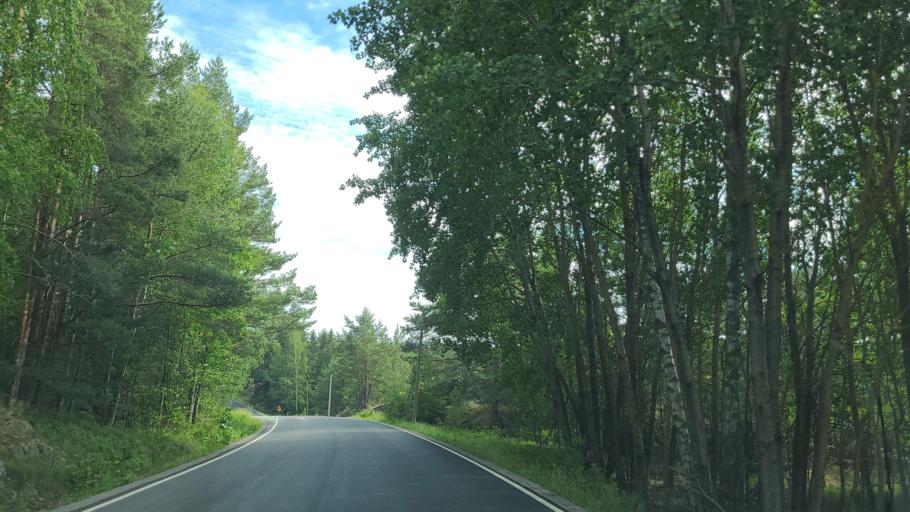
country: FI
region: Varsinais-Suomi
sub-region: Turku
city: Rymaettylae
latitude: 60.3224
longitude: 21.9559
